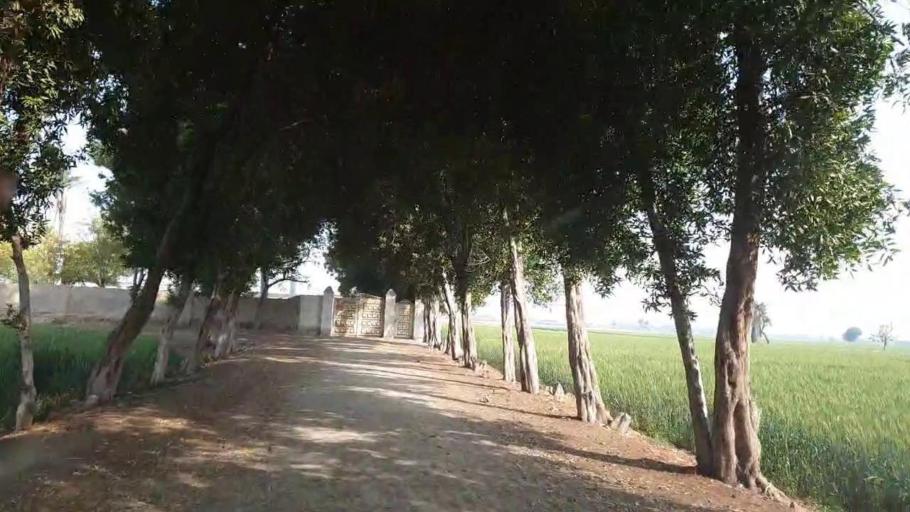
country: PK
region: Sindh
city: Mirpur Khas
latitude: 25.5134
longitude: 69.0337
